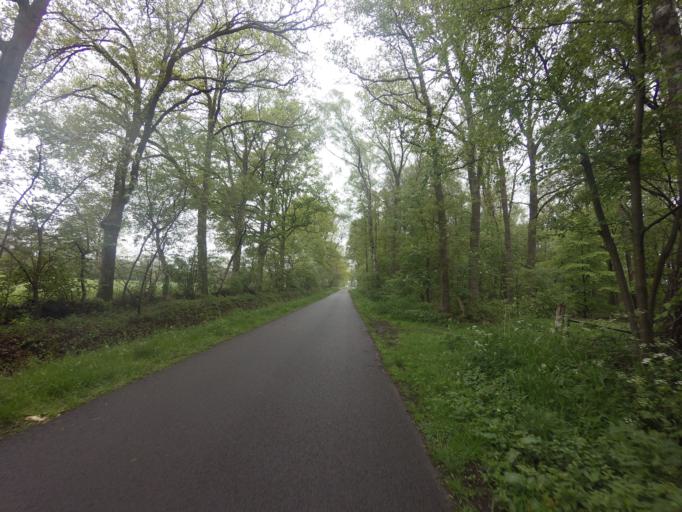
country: NL
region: Overijssel
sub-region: Gemeente Haaksbergen
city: Haaksbergen
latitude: 52.1279
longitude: 6.8165
